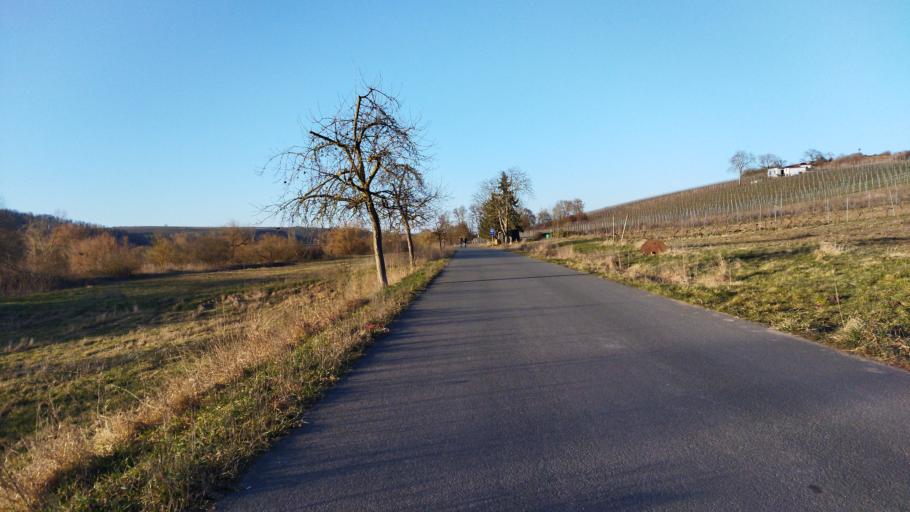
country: DE
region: Bavaria
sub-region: Regierungsbezirk Unterfranken
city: Mainstockheim
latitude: 49.7757
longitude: 10.1574
